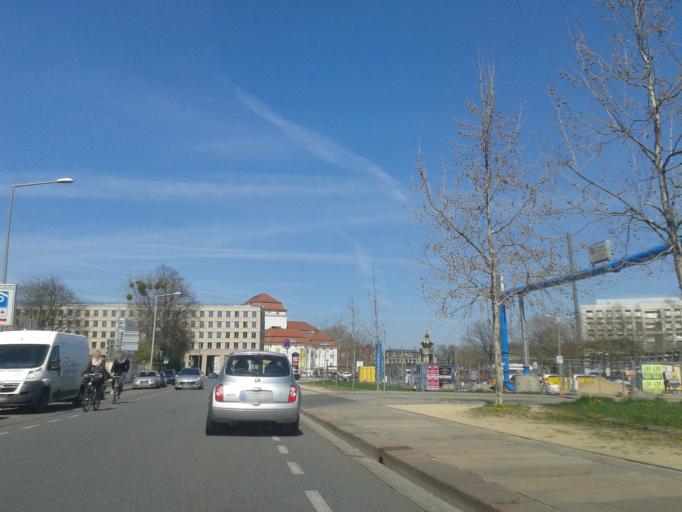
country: DE
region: Saxony
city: Dresden
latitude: 51.0491
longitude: 13.7329
